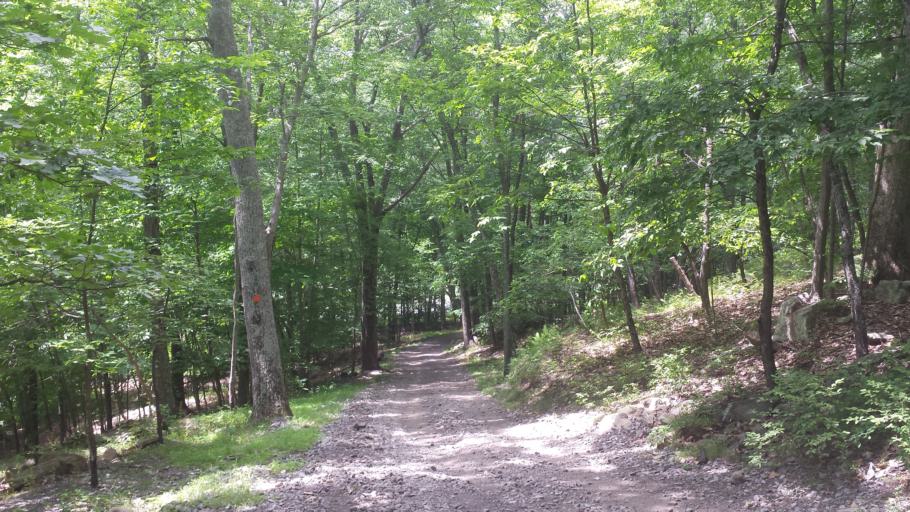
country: US
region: New York
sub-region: Putnam County
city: Peach Lake
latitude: 41.3100
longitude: -73.5746
